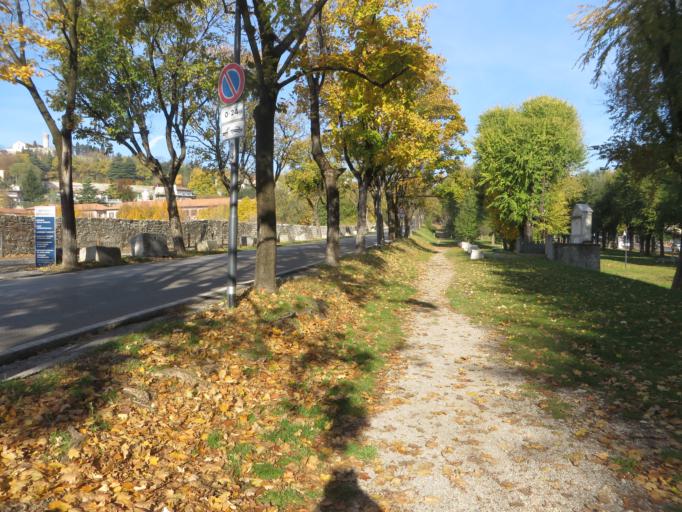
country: IT
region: Lombardy
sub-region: Provincia di Brescia
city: Brescia
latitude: 45.5393
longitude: 10.2312
